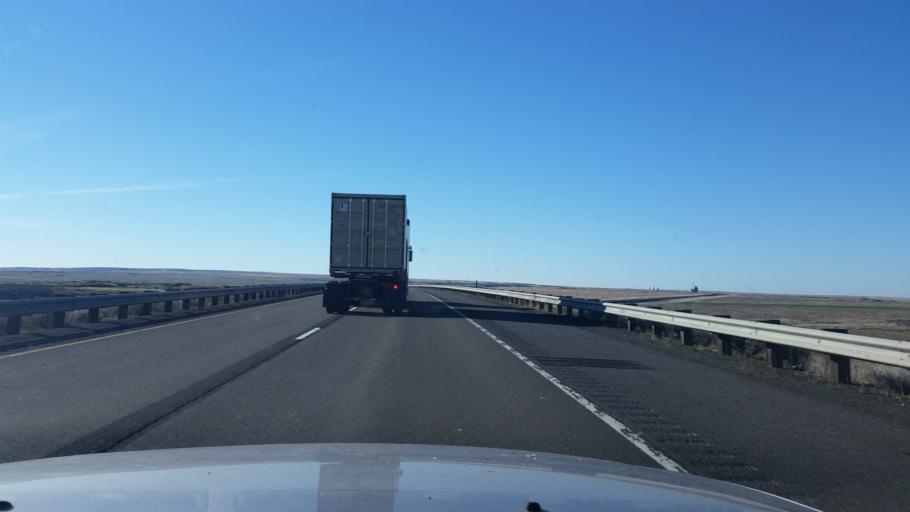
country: US
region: Washington
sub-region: Adams County
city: Ritzville
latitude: 47.2502
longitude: -118.1070
